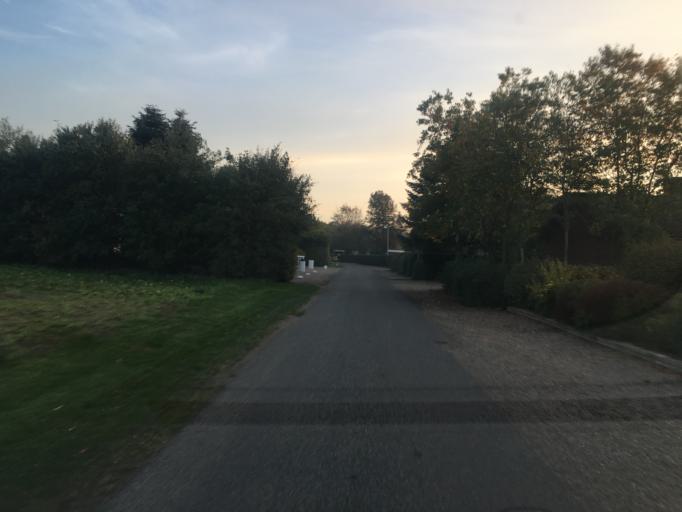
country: DK
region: South Denmark
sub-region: Aabenraa Kommune
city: Tinglev
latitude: 55.0124
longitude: 9.1229
